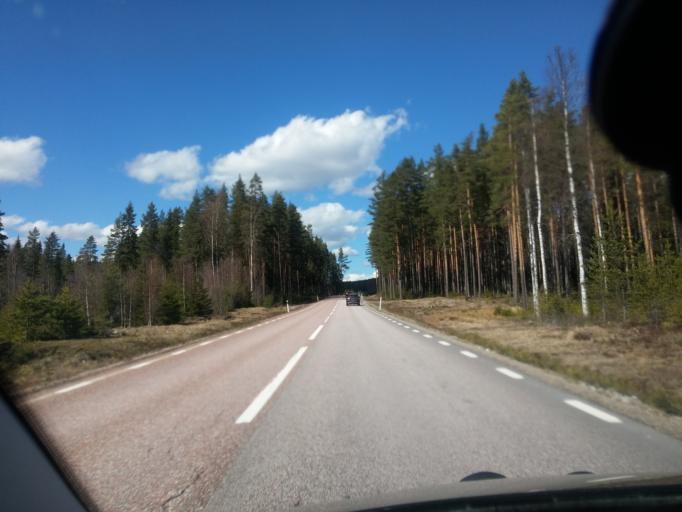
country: SE
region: Dalarna
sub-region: Faluns Kommun
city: Svardsjo
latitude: 60.7558
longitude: 15.7585
